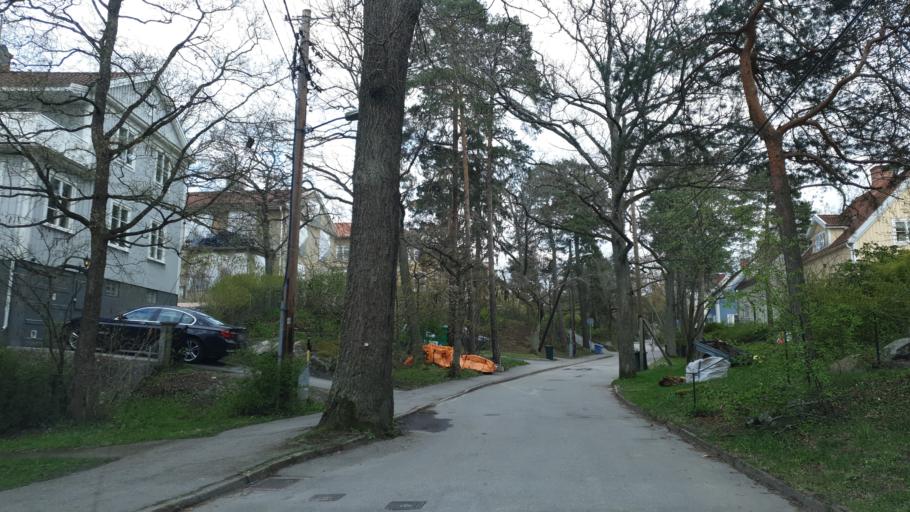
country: SE
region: Stockholm
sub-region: Sundbybergs Kommun
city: Sundbyberg
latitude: 59.3334
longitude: 17.9685
